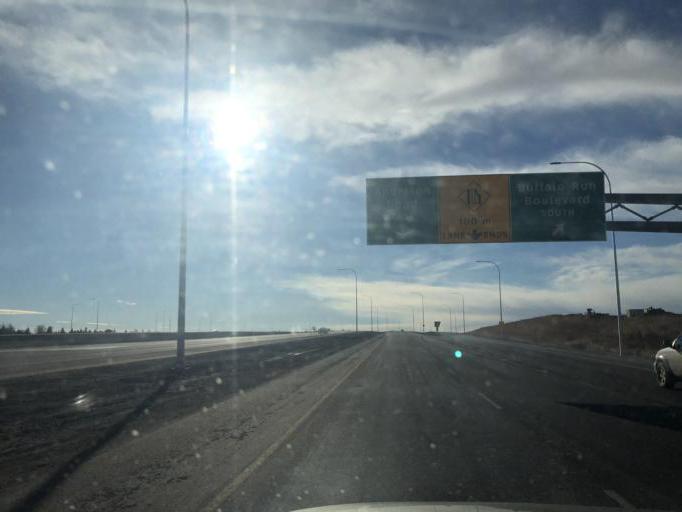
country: CA
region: Alberta
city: Calgary
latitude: 50.9575
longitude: -114.1435
